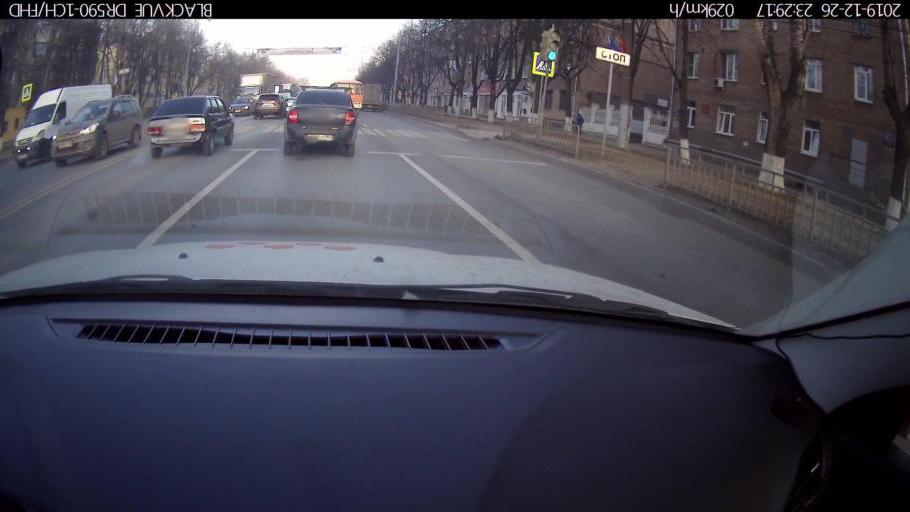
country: RU
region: Nizjnij Novgorod
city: Nizhniy Novgorod
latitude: 56.2631
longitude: 43.9094
